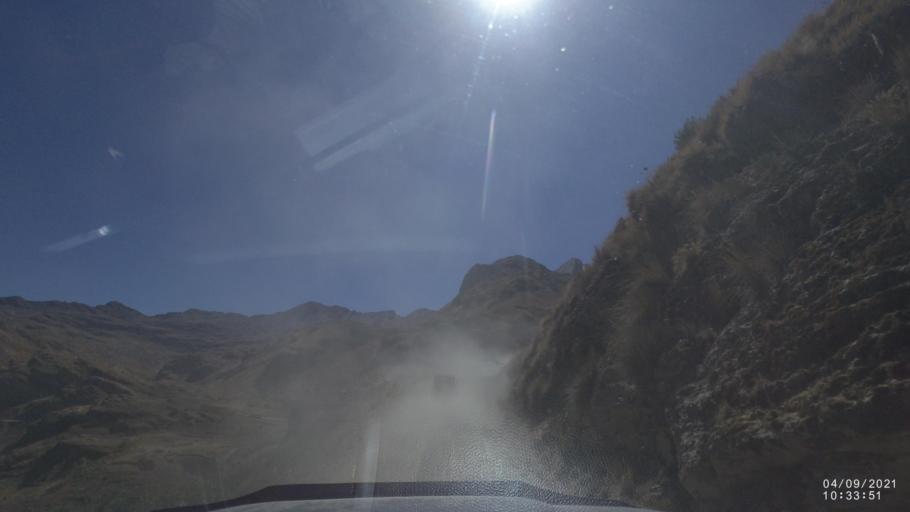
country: BO
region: Cochabamba
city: Sipe Sipe
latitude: -17.2938
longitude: -66.4463
